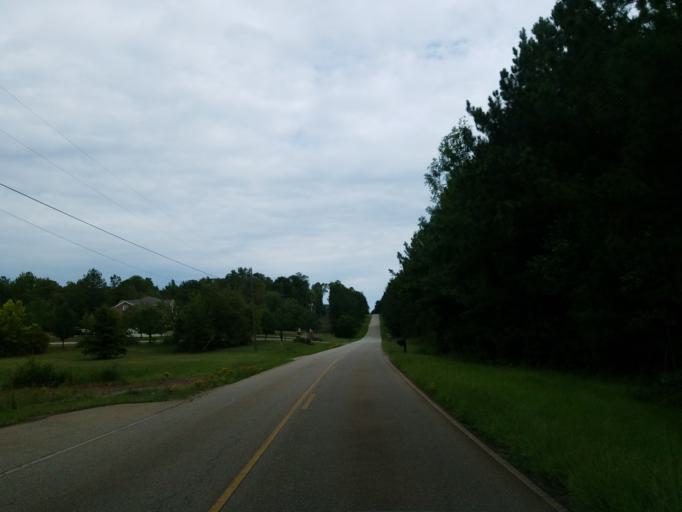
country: US
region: Georgia
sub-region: Bibb County
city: West Point
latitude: 32.9037
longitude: -83.8480
